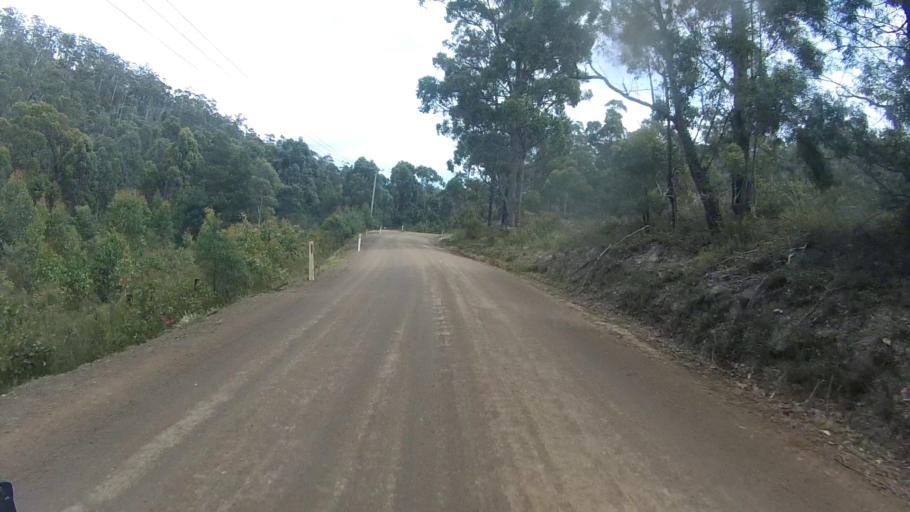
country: AU
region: Tasmania
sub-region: Sorell
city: Sorell
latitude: -42.7627
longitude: 147.8029
